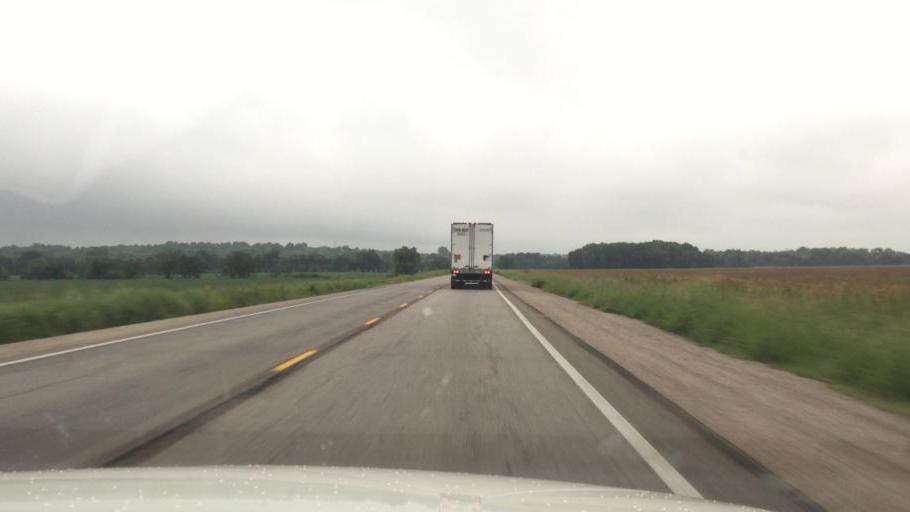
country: US
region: Kansas
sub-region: Montgomery County
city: Cherryvale
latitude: 37.1749
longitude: -95.5765
